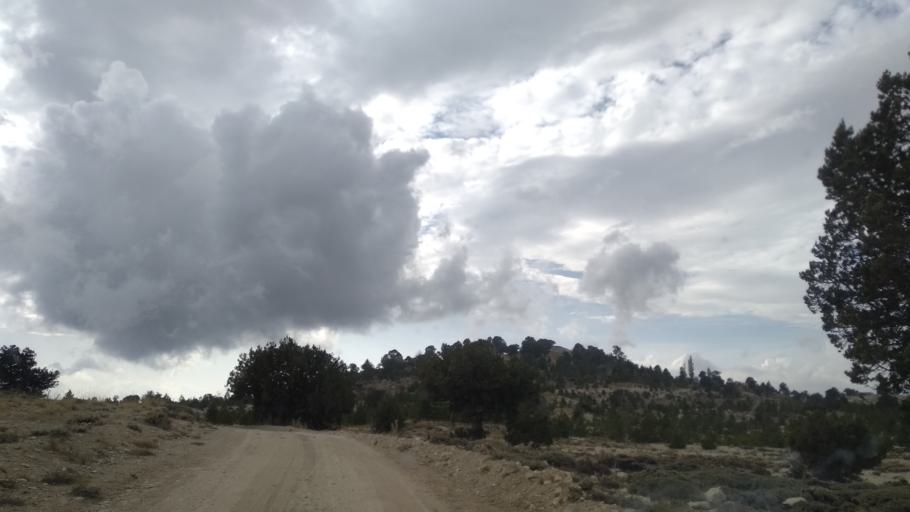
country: TR
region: Mersin
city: Sarikavak
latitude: 36.5748
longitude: 33.7560
